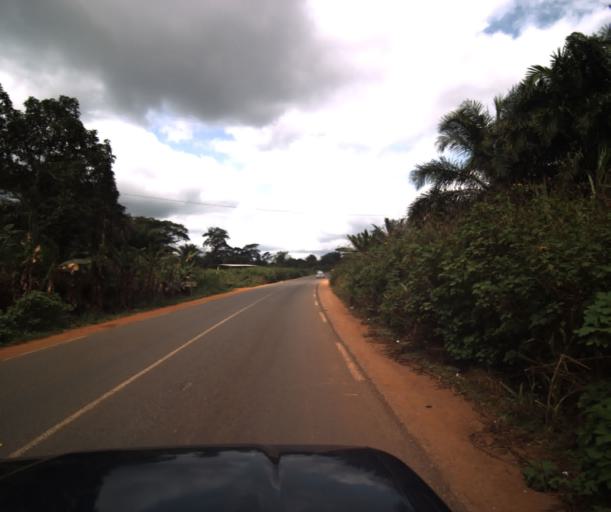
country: CM
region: Centre
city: Mbankomo
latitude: 3.7872
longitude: 11.4286
